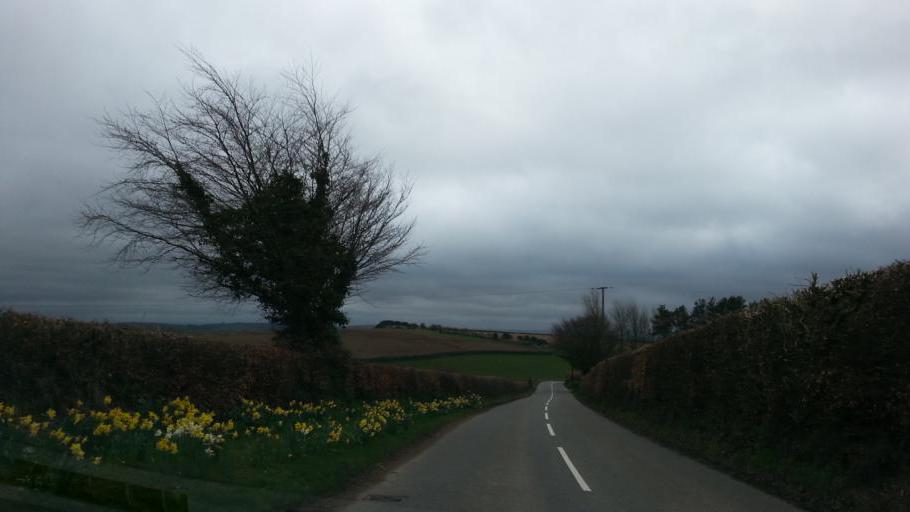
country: GB
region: England
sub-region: Devon
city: Barnstaple
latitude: 51.1087
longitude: -4.0211
